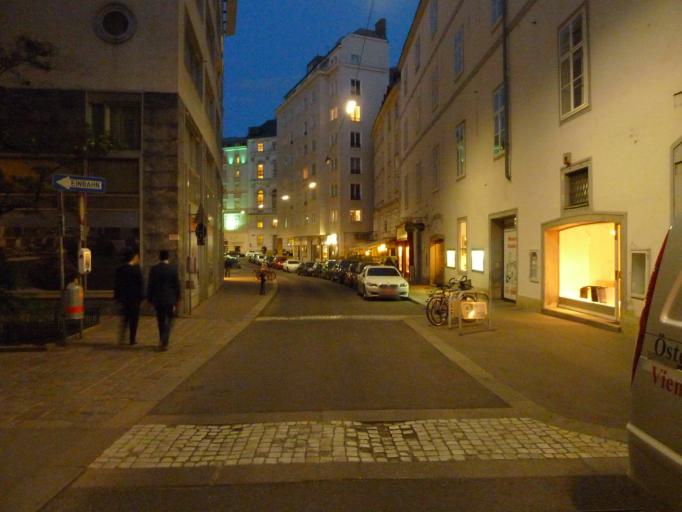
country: AT
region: Vienna
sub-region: Wien Stadt
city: Vienna
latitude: 48.2065
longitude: 16.3753
